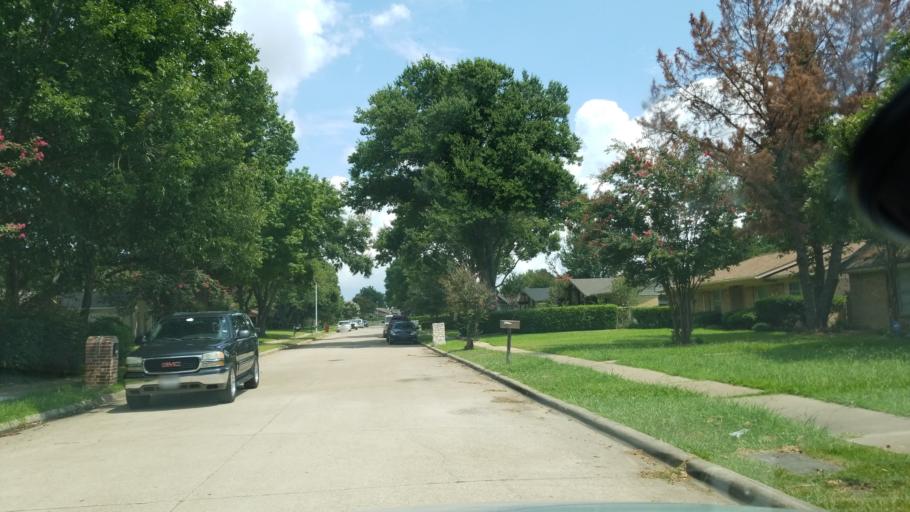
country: US
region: Texas
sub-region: Dallas County
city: Garland
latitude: 32.9293
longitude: -96.6557
